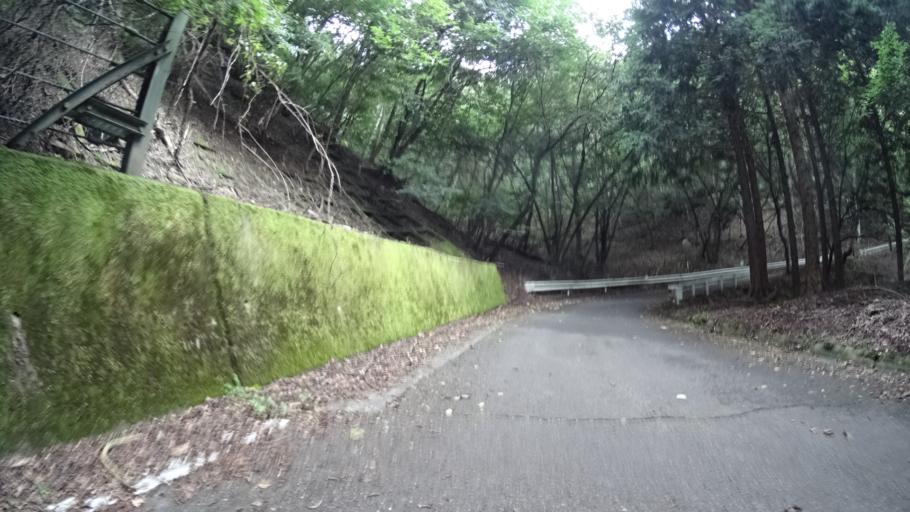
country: JP
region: Yamanashi
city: Enzan
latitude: 35.6148
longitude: 138.7786
